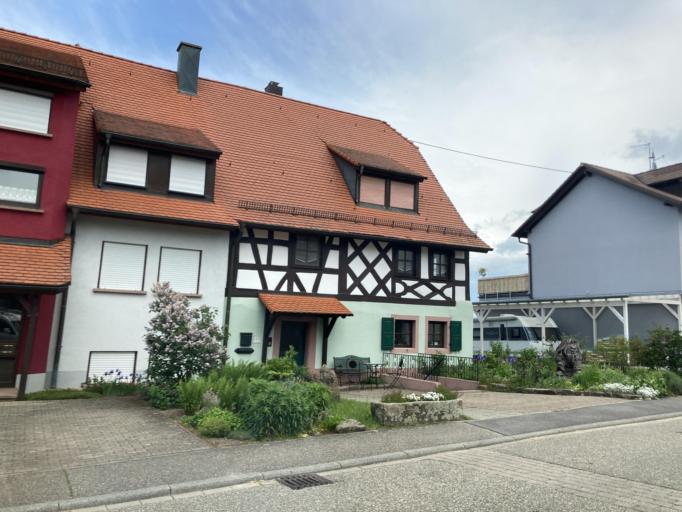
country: DE
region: Baden-Wuerttemberg
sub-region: Karlsruhe Region
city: Bad Herrenalb
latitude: 48.8443
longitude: 8.4508
